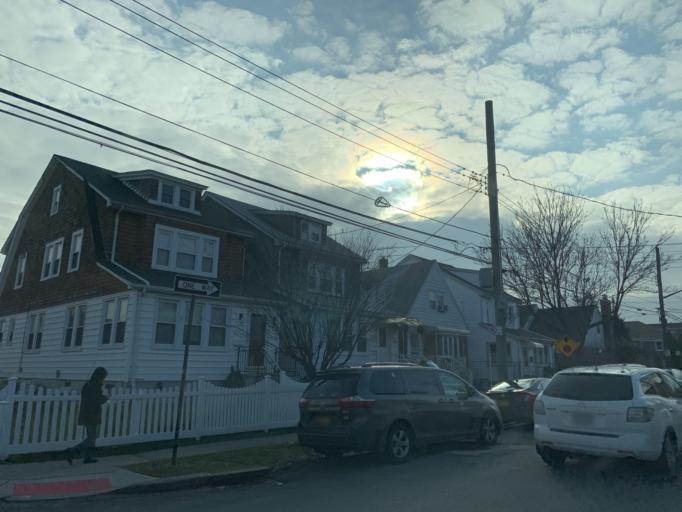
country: US
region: New York
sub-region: Queens County
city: Jamaica
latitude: 40.7448
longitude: -73.8274
